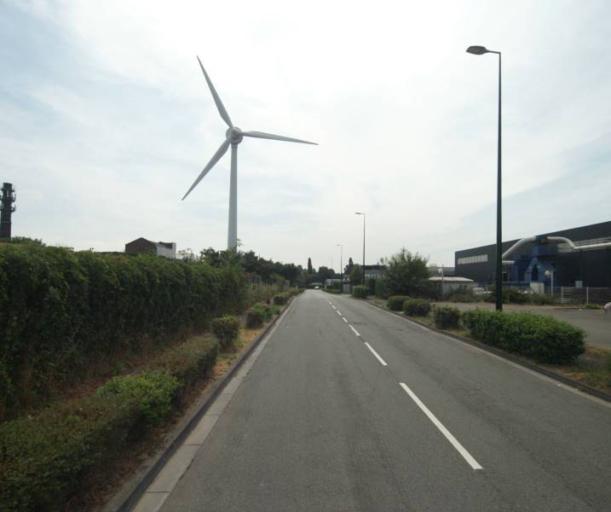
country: FR
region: Nord-Pas-de-Calais
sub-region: Departement du Nord
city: Mouvaux
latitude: 50.7182
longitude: 3.1307
